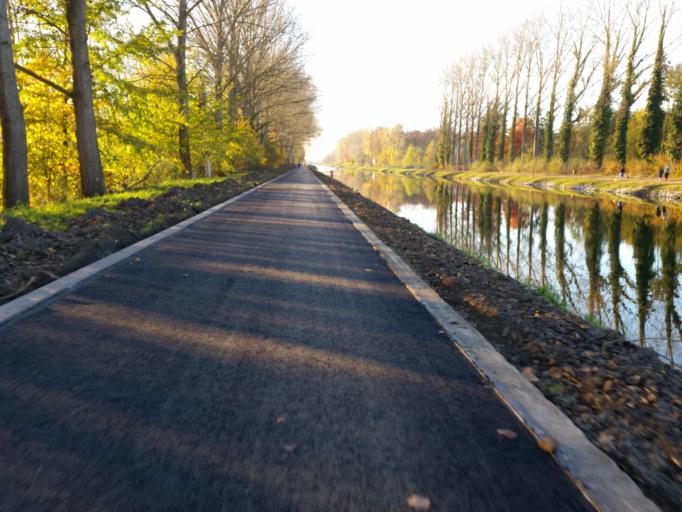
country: BE
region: Flanders
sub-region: Provincie Vlaams-Brabant
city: Haacht
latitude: 50.9478
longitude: 4.6392
